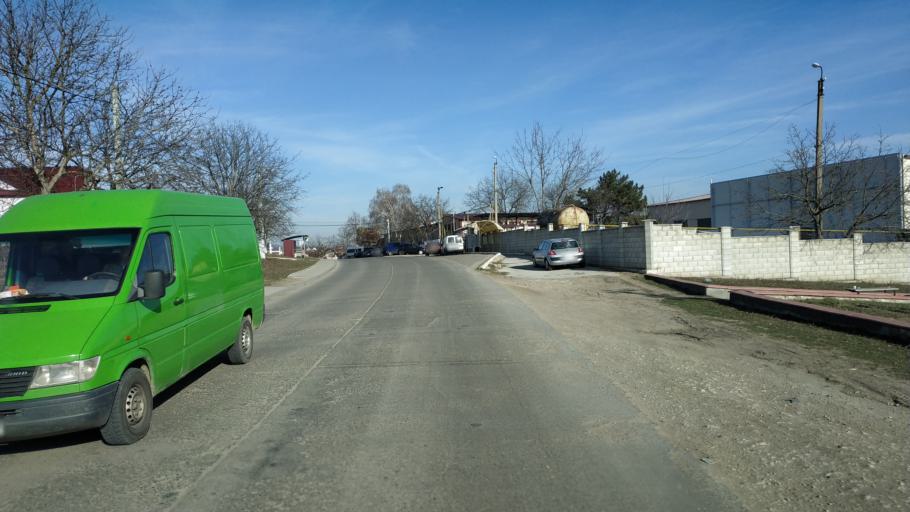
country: MD
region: Chisinau
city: Vatra
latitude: 47.0036
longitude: 28.6714
